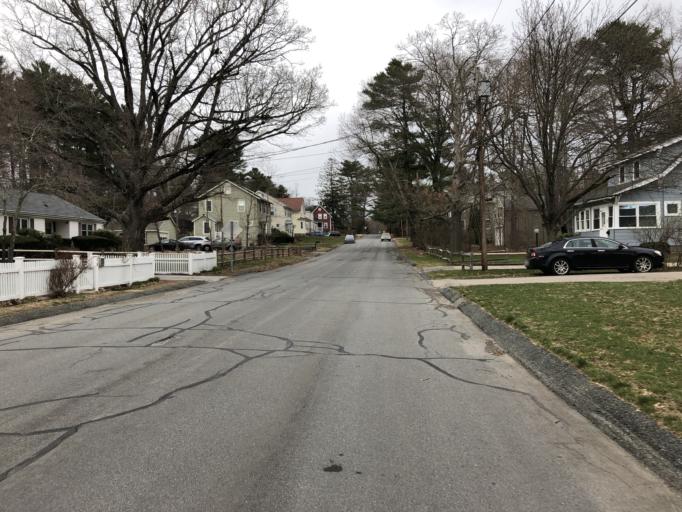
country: US
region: Massachusetts
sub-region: Norfolk County
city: Stoughton
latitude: 42.1230
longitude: -71.0934
